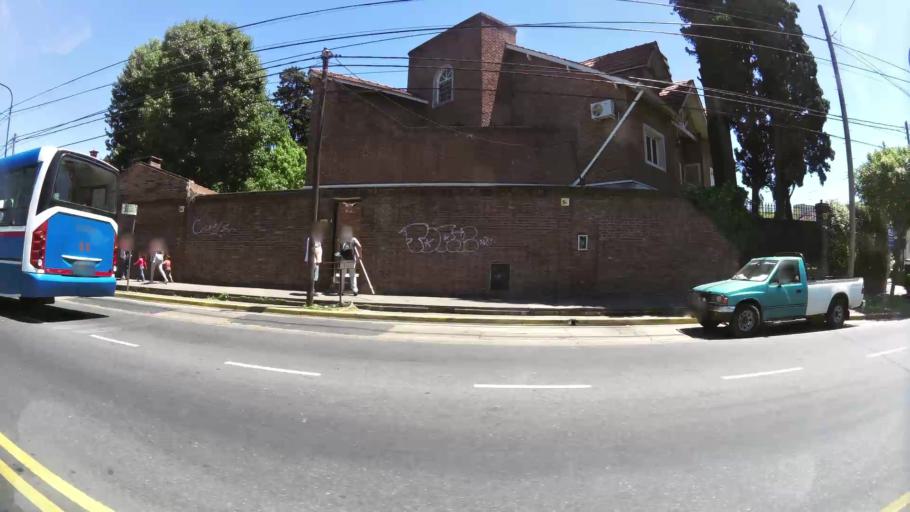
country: AR
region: Buenos Aires
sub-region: Partido de San Isidro
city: San Isidro
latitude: -34.5007
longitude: -58.5589
